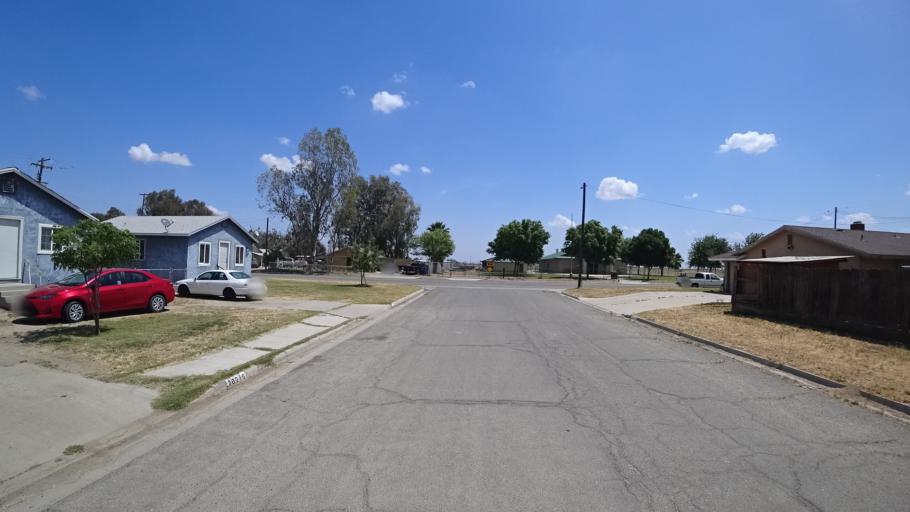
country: US
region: California
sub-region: Kings County
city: Stratford
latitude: 36.1882
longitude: -119.8209
